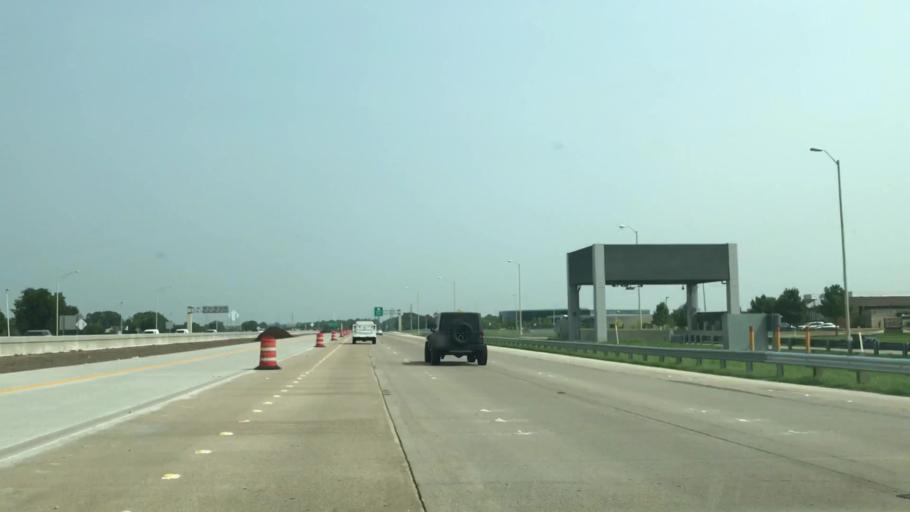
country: US
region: Texas
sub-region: Dallas County
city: Sachse
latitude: 32.9633
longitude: -96.6388
